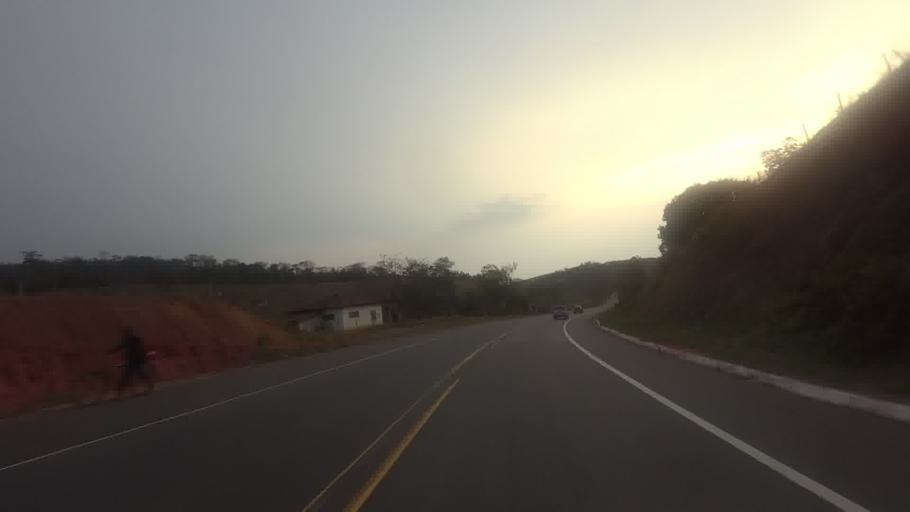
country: BR
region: Rio de Janeiro
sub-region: Carmo
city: Carmo
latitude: -21.7785
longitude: -42.5372
